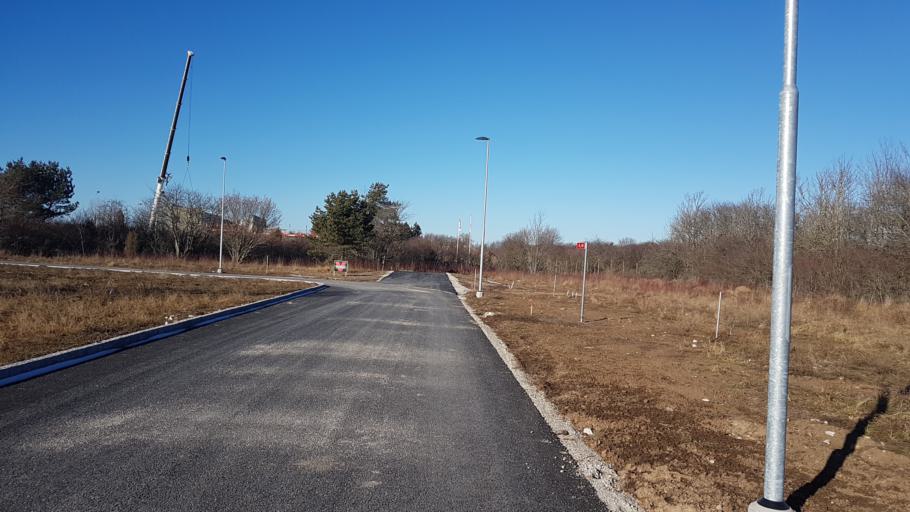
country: SE
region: Gotland
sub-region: Gotland
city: Visby
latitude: 57.6272
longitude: 18.3117
